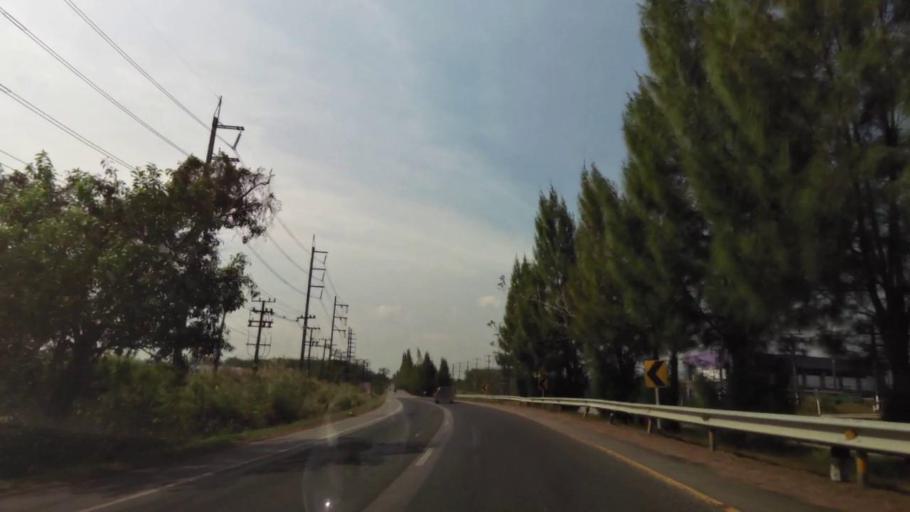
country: TH
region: Chanthaburi
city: Chanthaburi
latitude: 12.6632
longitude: 102.1193
